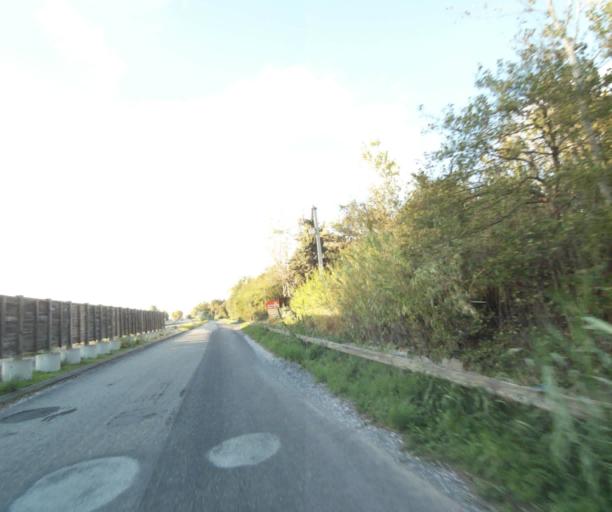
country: FR
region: Languedoc-Roussillon
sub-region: Departement des Pyrenees-Orientales
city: Sant Andreu de Sureda
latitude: 42.5728
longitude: 2.9972
